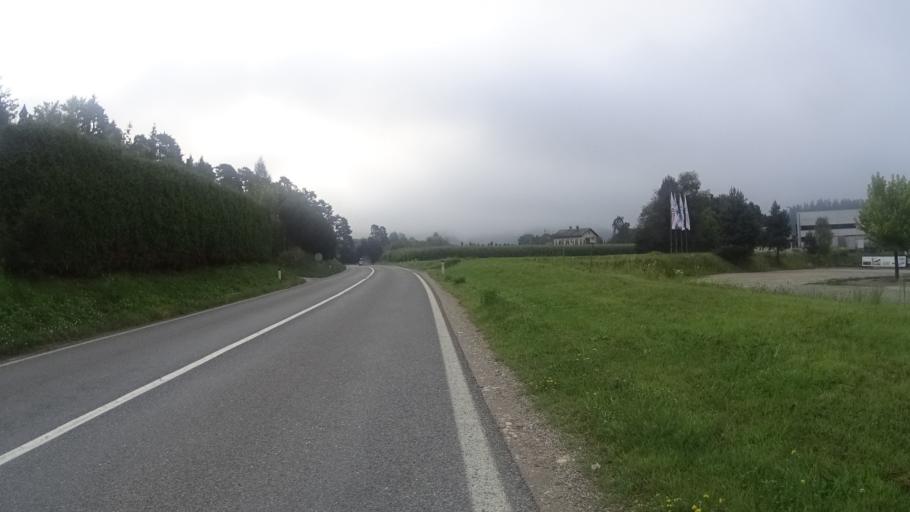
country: SI
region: Vuzenica
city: Vuzenica
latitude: 46.5984
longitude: 15.1512
